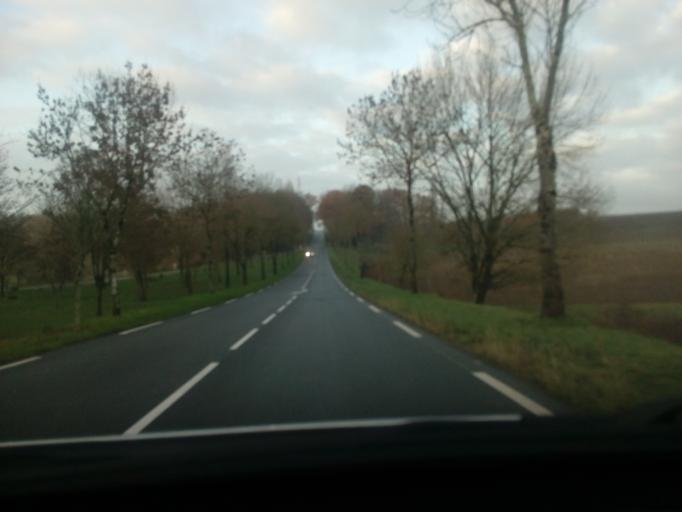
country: FR
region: Poitou-Charentes
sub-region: Departement de la Charente-Maritime
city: Jonzac
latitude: 45.4441
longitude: -0.4061
